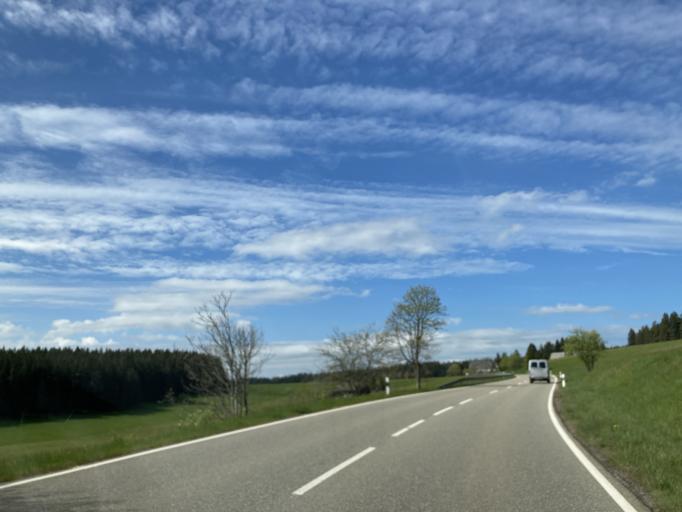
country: DE
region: Baden-Wuerttemberg
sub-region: Freiburg Region
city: Schonwald im Schwarzwald
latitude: 48.0929
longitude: 8.2034
